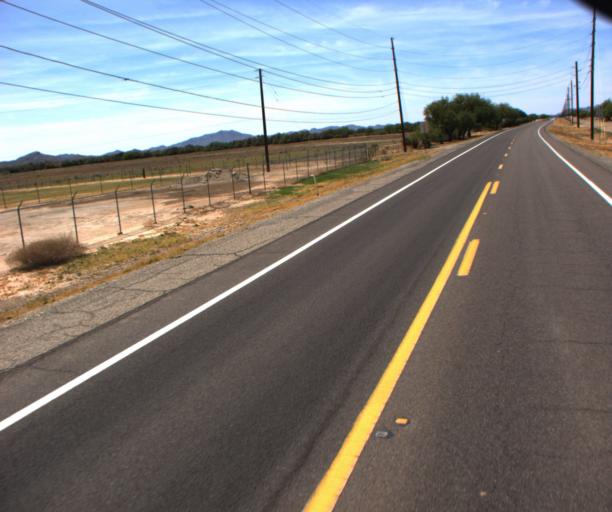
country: US
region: Arizona
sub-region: La Paz County
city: Salome
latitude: 33.8201
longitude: -113.5457
